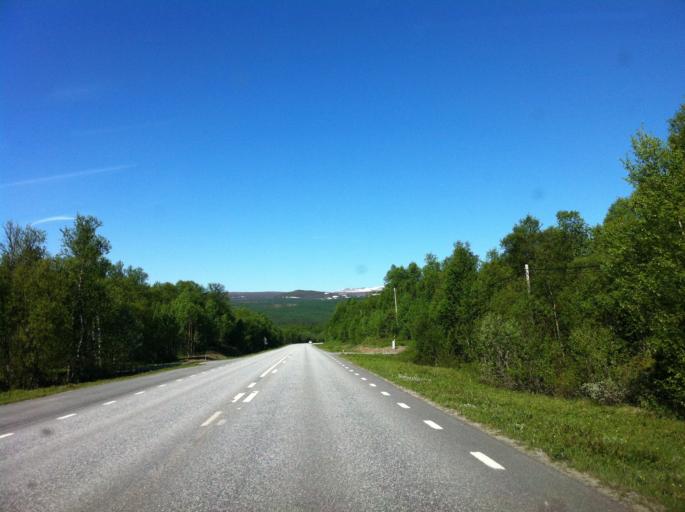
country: NO
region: Hedmark
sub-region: Engerdal
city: Engerdal
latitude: 62.5347
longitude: 12.3856
